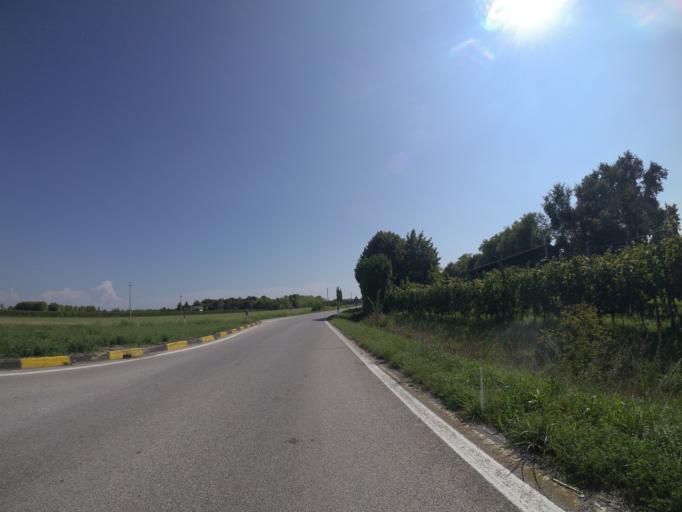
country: IT
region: Friuli Venezia Giulia
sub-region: Provincia di Udine
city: Carlino
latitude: 45.8081
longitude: 13.1646
